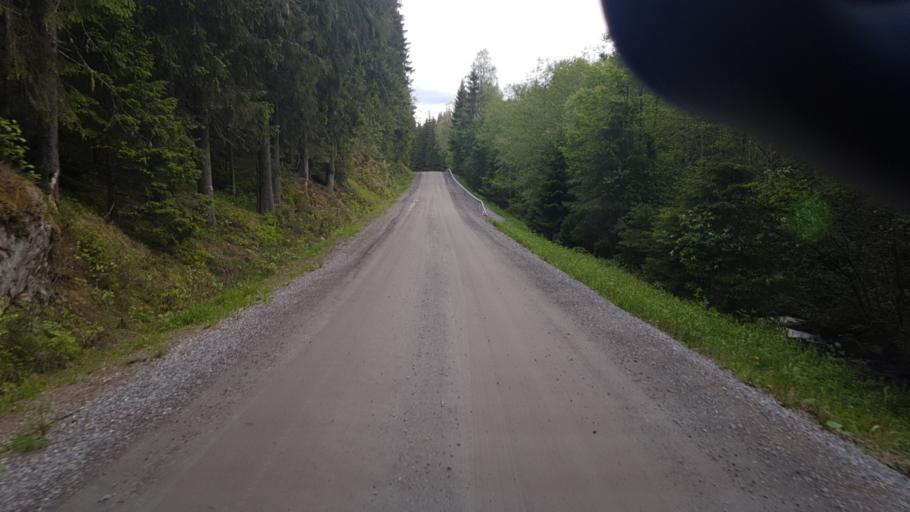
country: NO
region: Ostfold
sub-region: Romskog
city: Romskog
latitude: 59.7110
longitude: 11.9835
